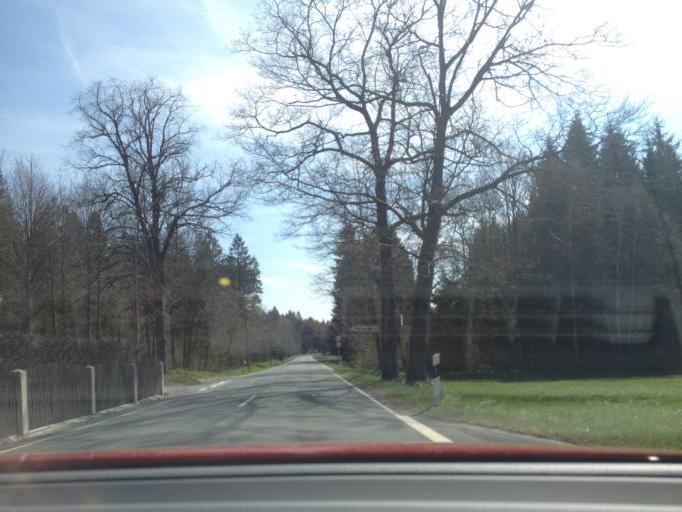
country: DE
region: Bavaria
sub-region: Upper Franconia
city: Oberhaid
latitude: 50.0965
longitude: 11.8178
